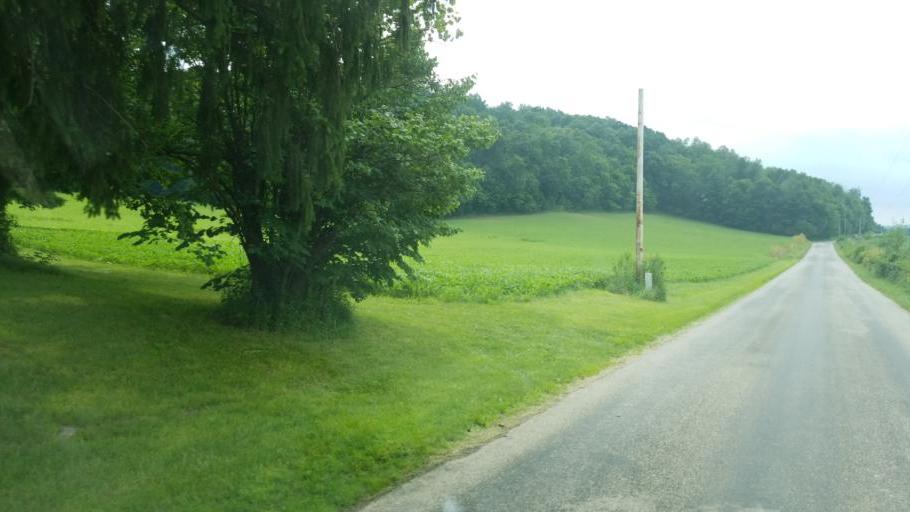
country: US
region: Ohio
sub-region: Licking County
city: Utica
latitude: 40.1708
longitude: -82.4305
